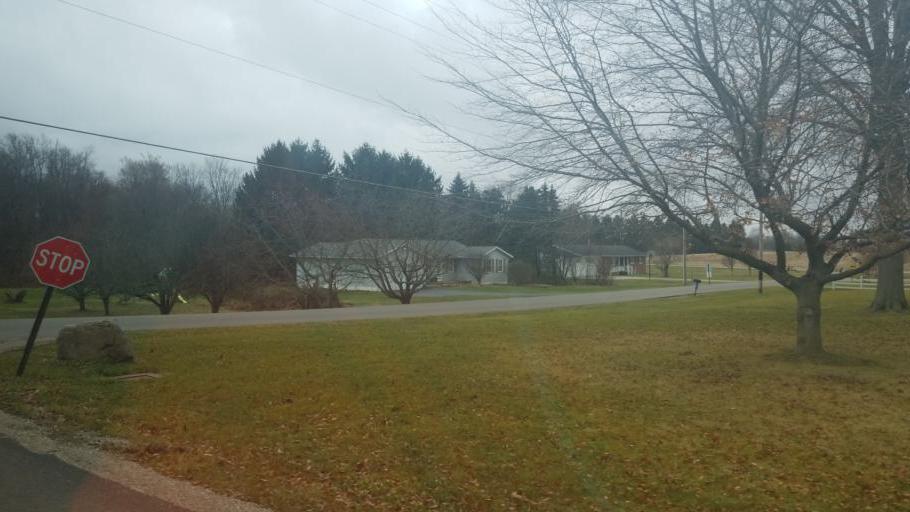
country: US
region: Ohio
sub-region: Crawford County
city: Galion
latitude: 40.7231
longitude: -82.8186
